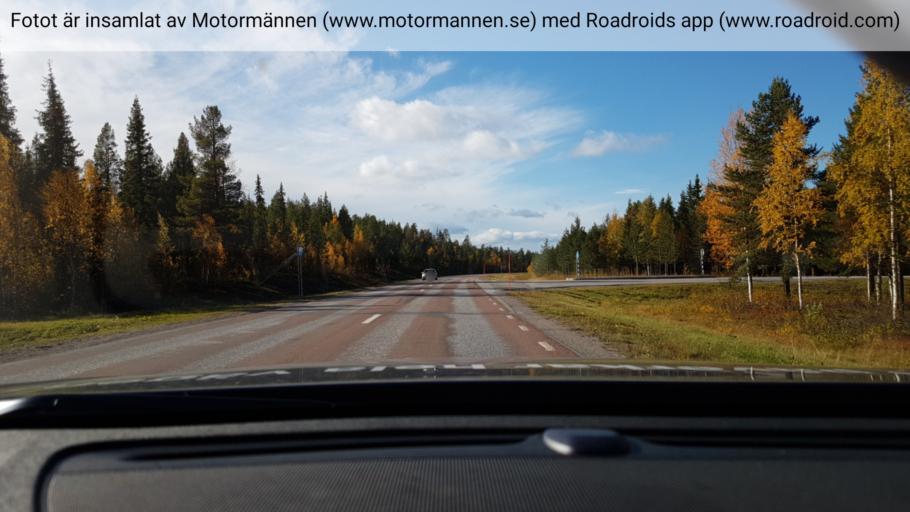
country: SE
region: Norrbotten
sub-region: Arjeplogs Kommun
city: Arjeplog
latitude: 66.0543
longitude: 17.9249
